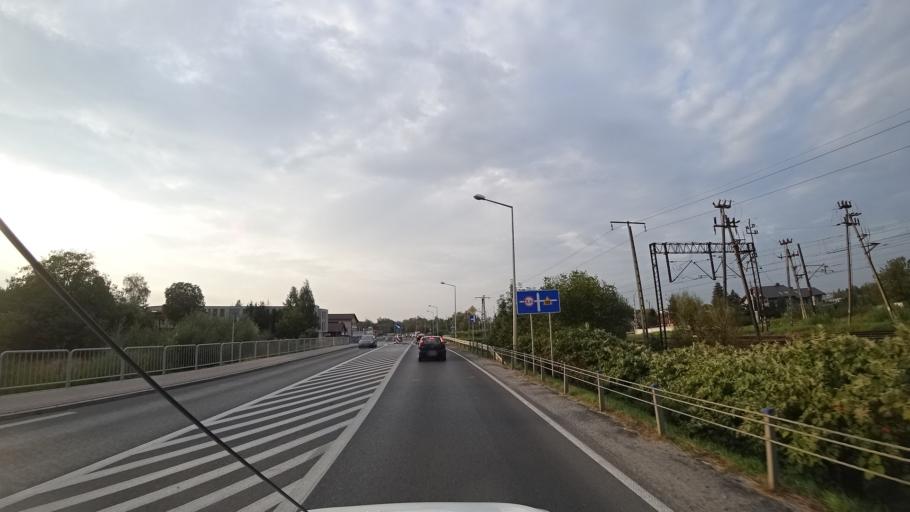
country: PL
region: Lesser Poland Voivodeship
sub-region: Powiat wadowicki
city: Wadowice
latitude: 49.8877
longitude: 19.4987
